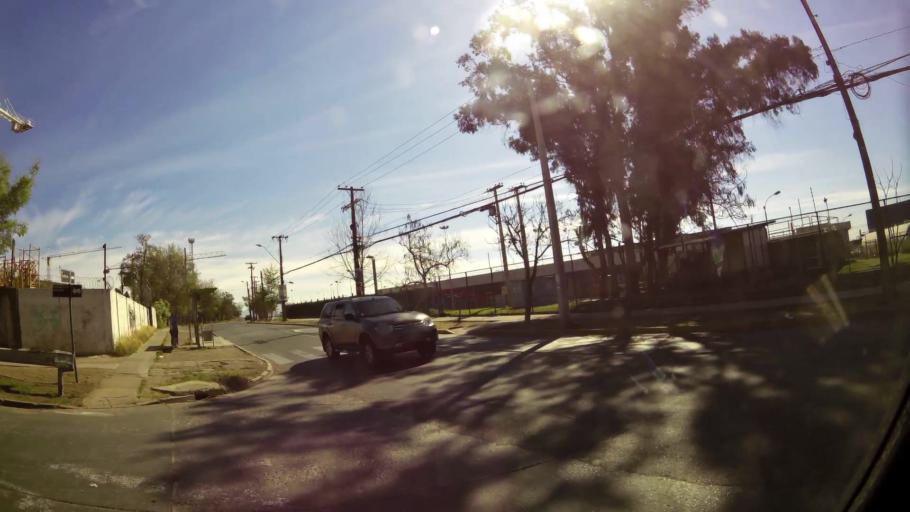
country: CL
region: Santiago Metropolitan
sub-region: Provincia de Santiago
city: Lo Prado
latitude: -33.4913
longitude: -70.7196
